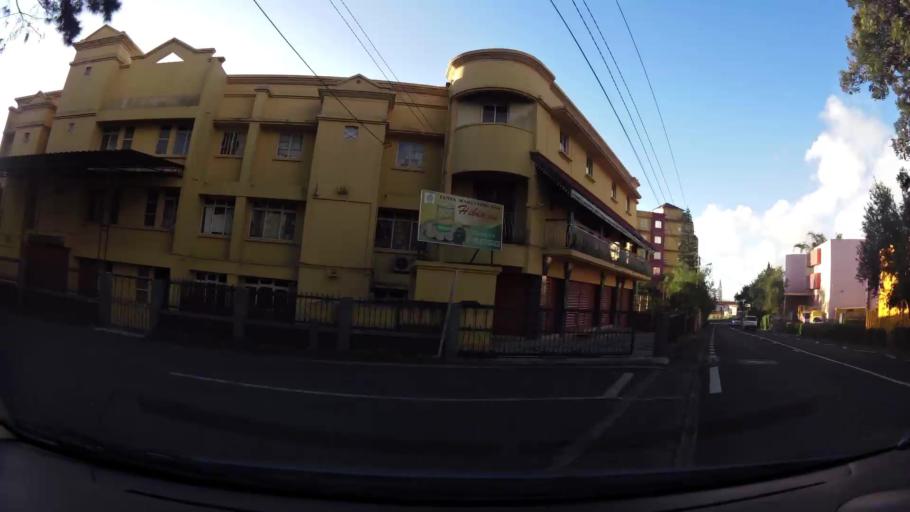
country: MU
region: Plaines Wilhems
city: Curepipe
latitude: -20.3079
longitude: 57.5252
